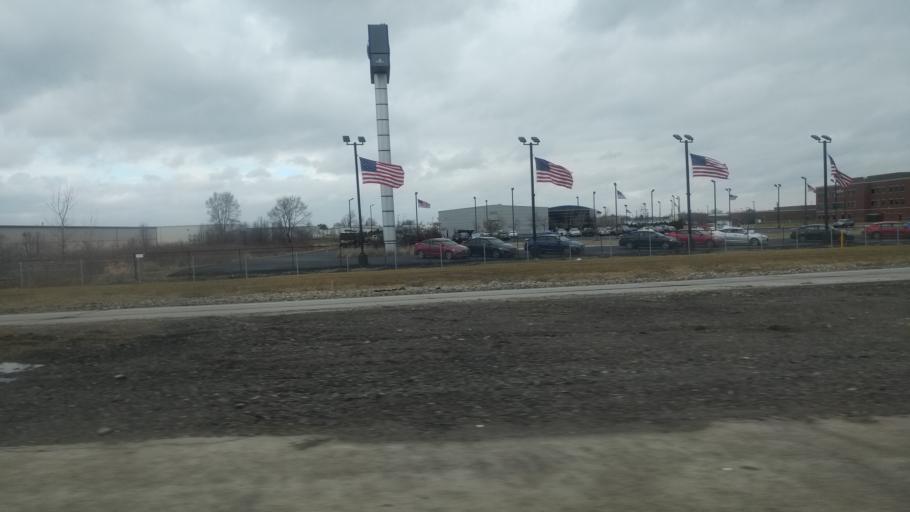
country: US
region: Ohio
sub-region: Wood County
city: Perrysburg
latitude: 41.5328
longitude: -83.6394
